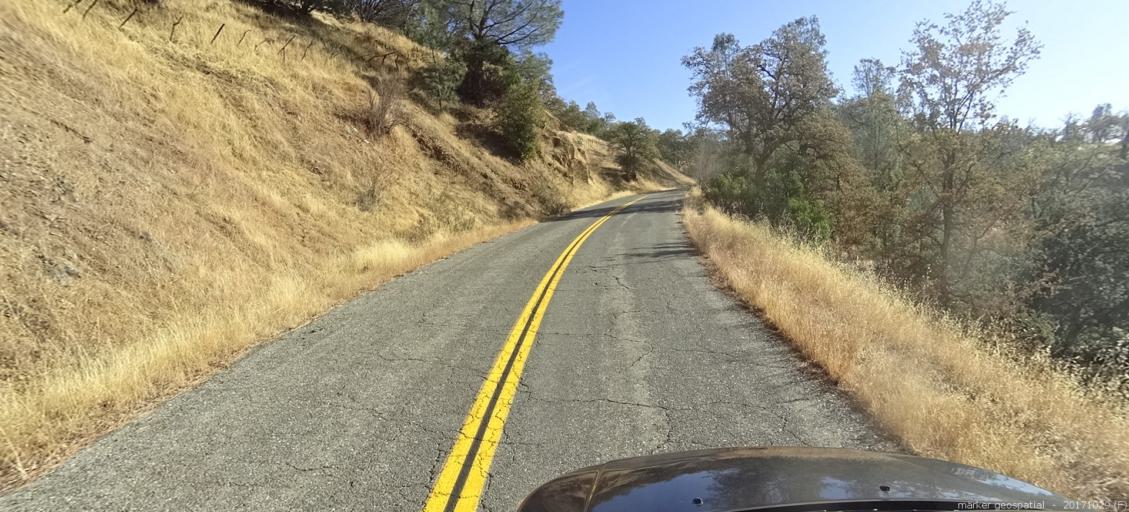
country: US
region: California
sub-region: Trinity County
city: Lewiston
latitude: 40.4027
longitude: -122.7770
